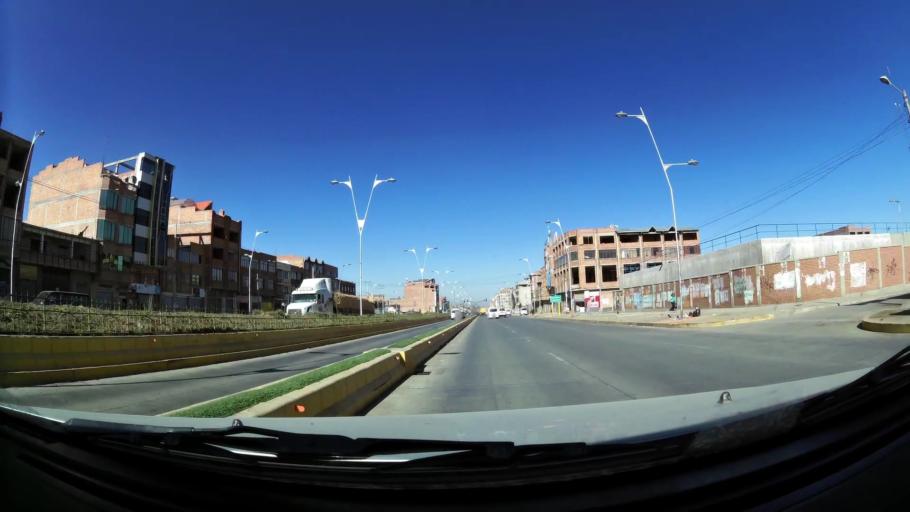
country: BO
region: La Paz
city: La Paz
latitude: -16.5312
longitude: -68.1871
